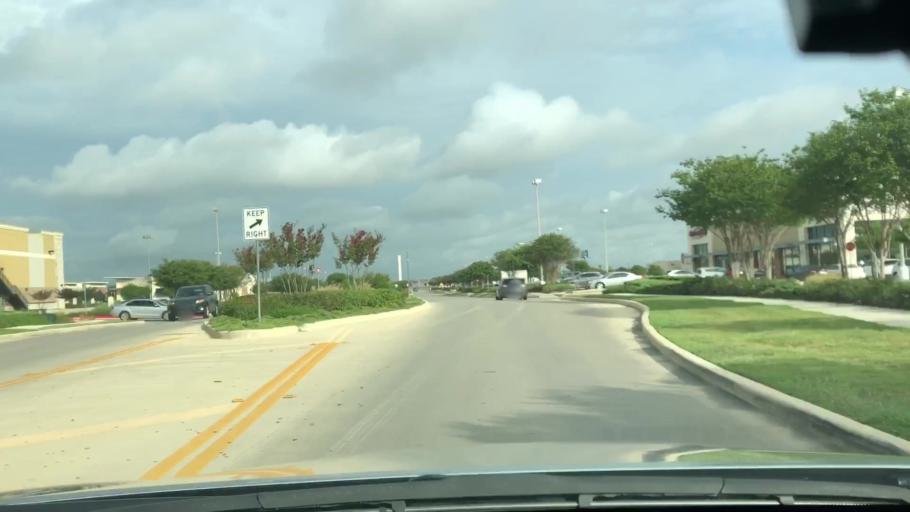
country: US
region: Texas
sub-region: Guadalupe County
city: Lake Dunlap
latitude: 29.7276
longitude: -98.0717
